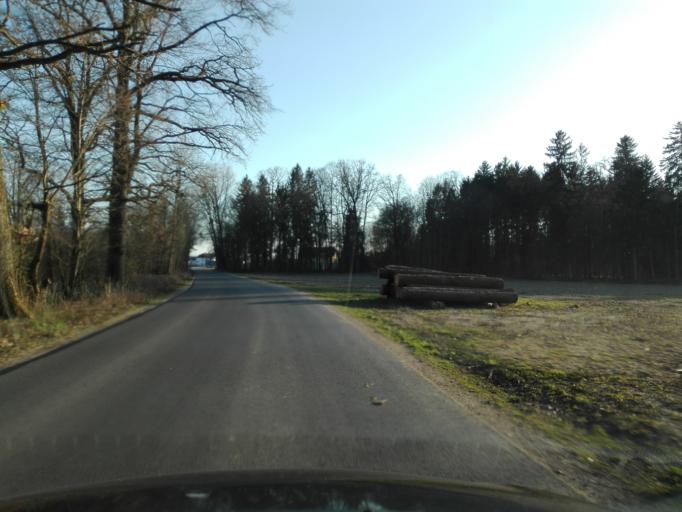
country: AT
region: Upper Austria
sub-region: Politischer Bezirk Perg
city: Perg
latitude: 48.2096
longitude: 14.6900
